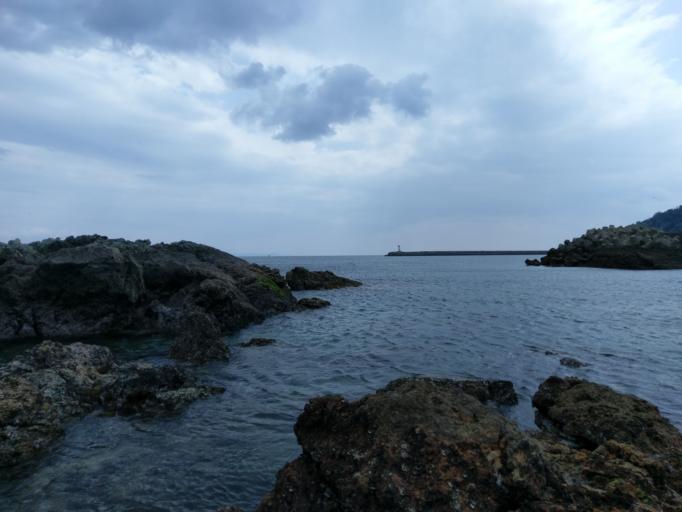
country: JP
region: Nagasaki
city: Nagasaki-shi
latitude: 32.7062
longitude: 129.9214
